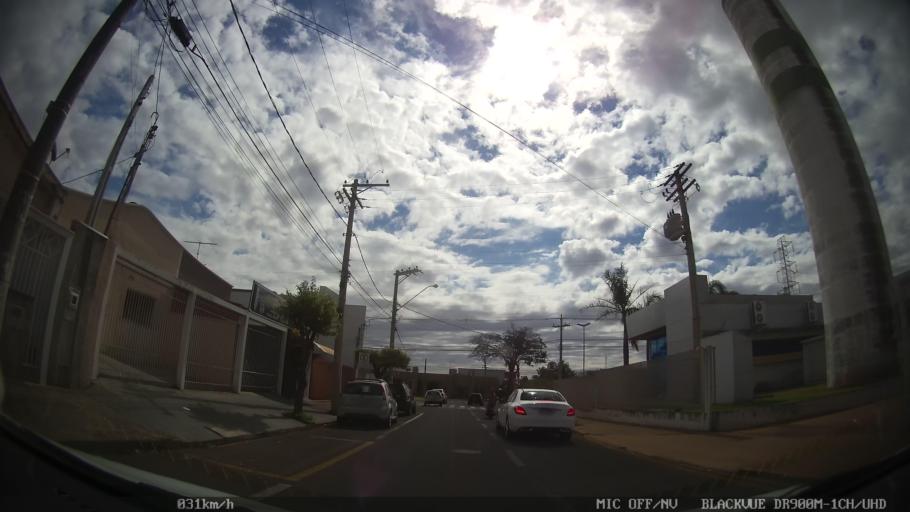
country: BR
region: Sao Paulo
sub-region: Bady Bassitt
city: Bady Bassitt
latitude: -20.8126
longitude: -49.5071
